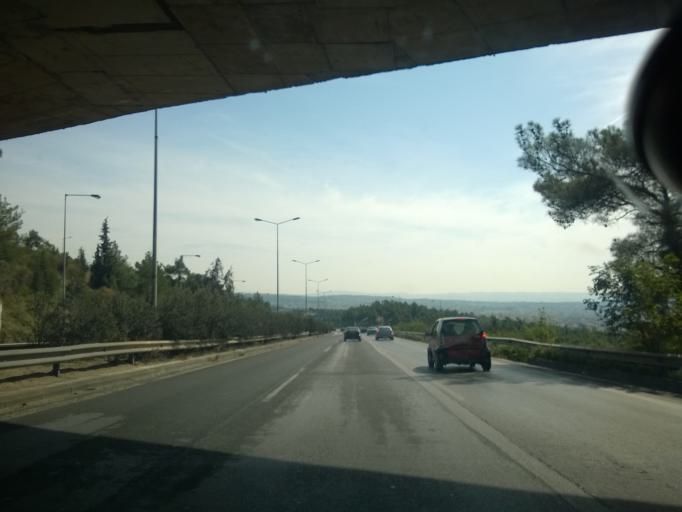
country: GR
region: Central Macedonia
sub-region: Nomos Thessalonikis
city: Agios Pavlos
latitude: 40.6332
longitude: 22.9732
